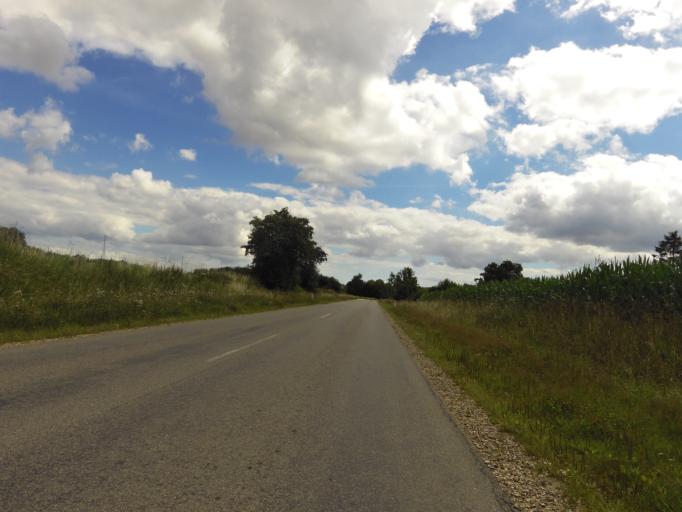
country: DK
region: South Denmark
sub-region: Haderslev Kommune
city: Haderslev
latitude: 55.2773
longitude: 9.4169
